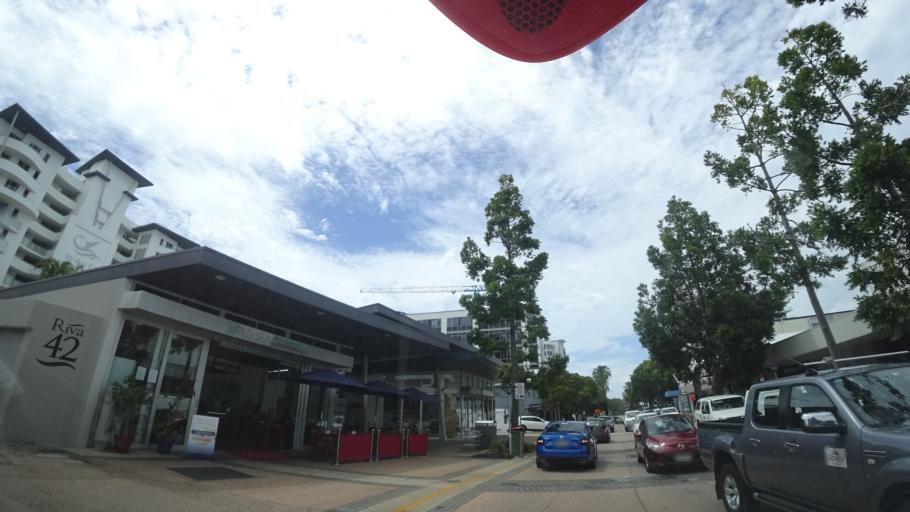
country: AU
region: Queensland
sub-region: Sunshine Coast
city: Mooloolaba
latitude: -26.6518
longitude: 153.0924
